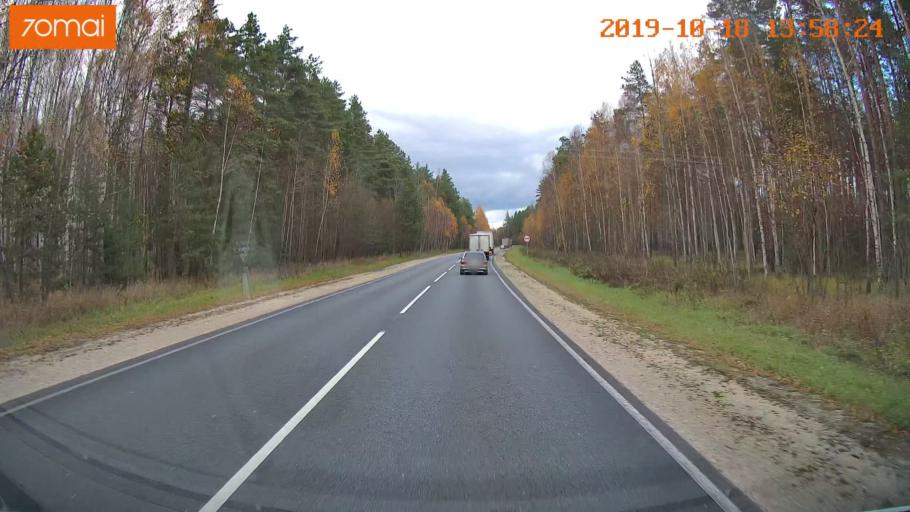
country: RU
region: Rjazan
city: Spas-Klepiki
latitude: 55.0845
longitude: 40.0540
